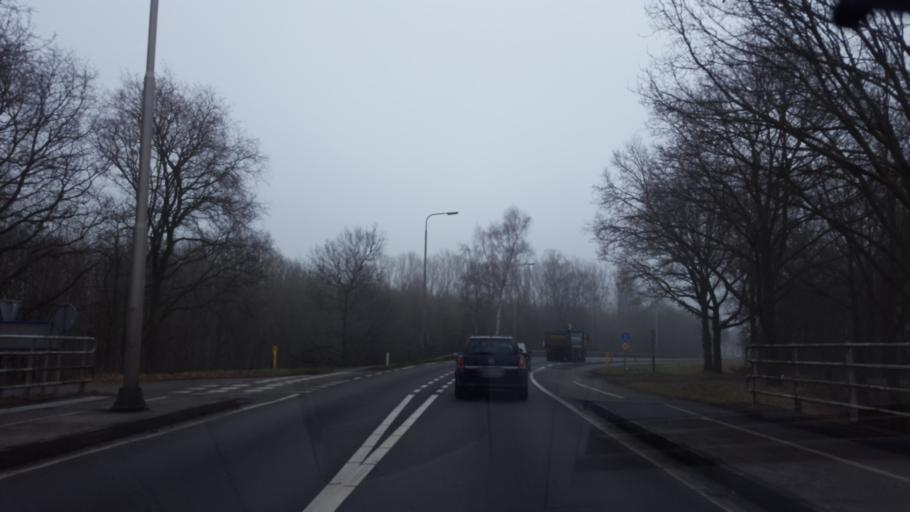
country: NL
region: Limburg
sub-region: Gemeente Leudal
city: Kelpen-Oler
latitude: 51.2352
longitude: 5.7979
